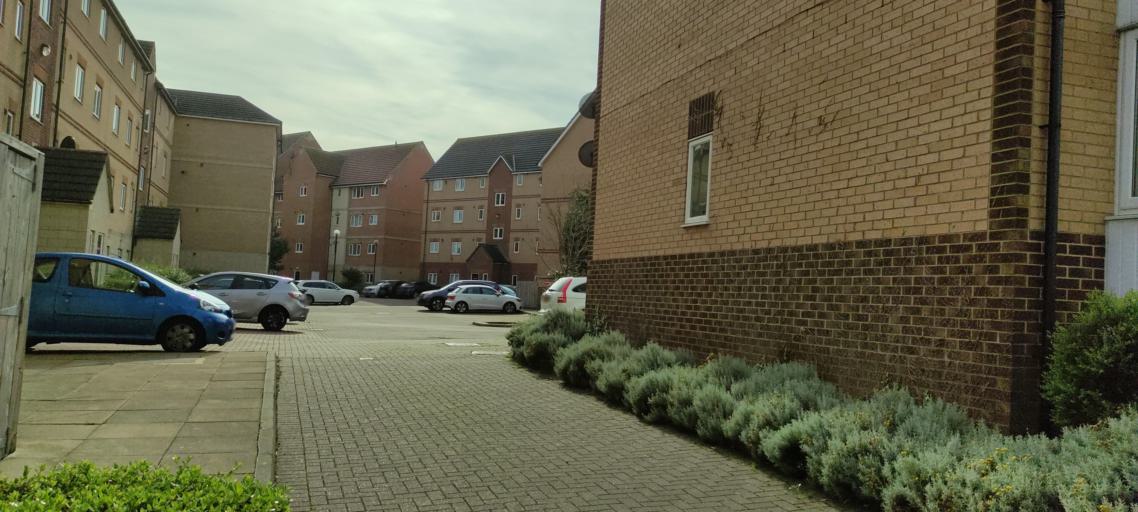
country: GB
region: England
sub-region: Hartlepool
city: Hartlepool
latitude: 54.6886
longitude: -1.2004
